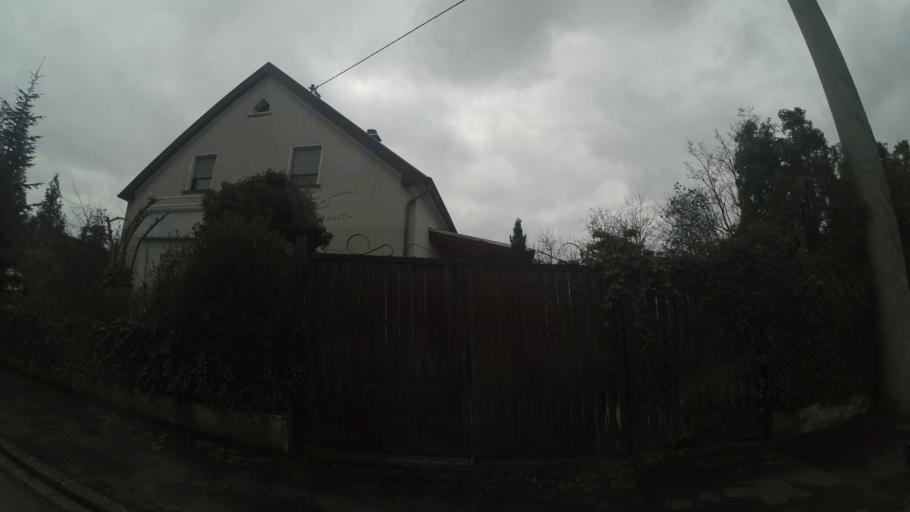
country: DE
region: Saarland
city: Ensdorf
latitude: 49.3048
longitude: 6.7870
